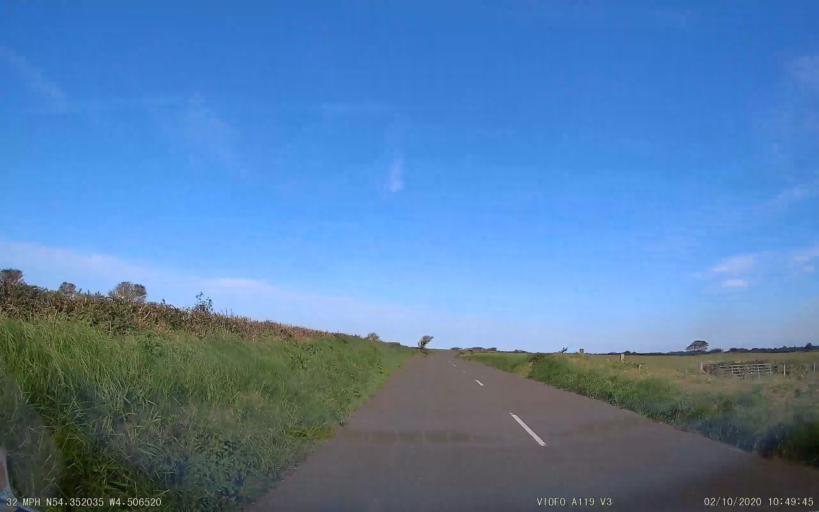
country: IM
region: Ramsey
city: Ramsey
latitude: 54.3520
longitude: -4.5065
